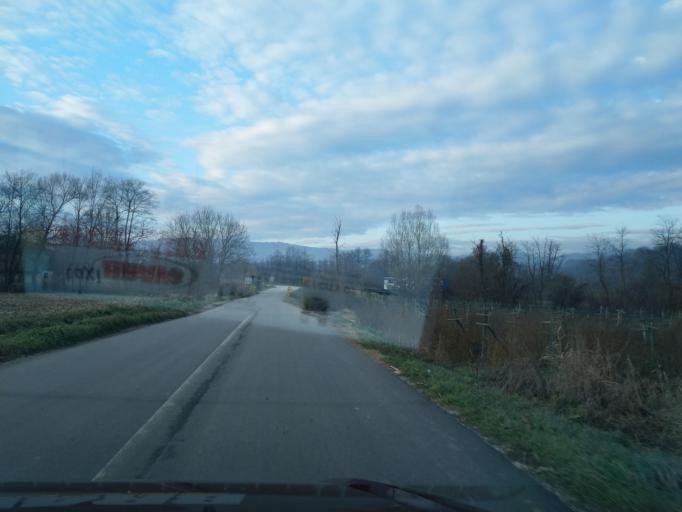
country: RS
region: Central Serbia
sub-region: Zlatiborski Okrug
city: Kosjeric
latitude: 43.9231
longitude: 19.9011
